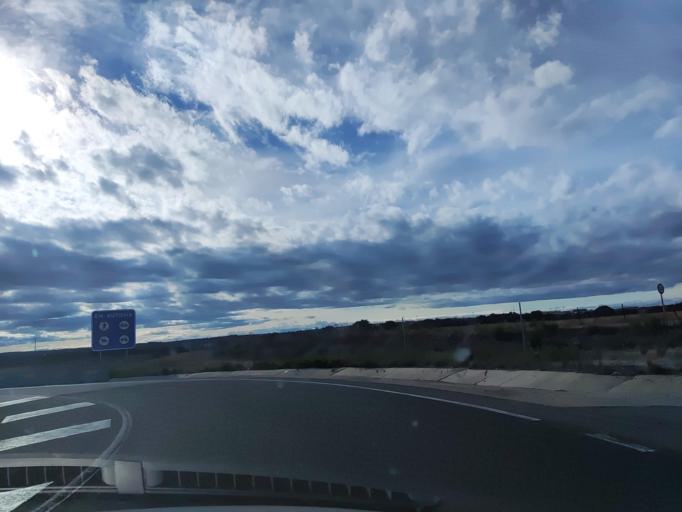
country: ES
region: Castille and Leon
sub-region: Provincia de Salamanca
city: Fuentes de Onoro
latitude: 40.5947
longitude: -6.7968
